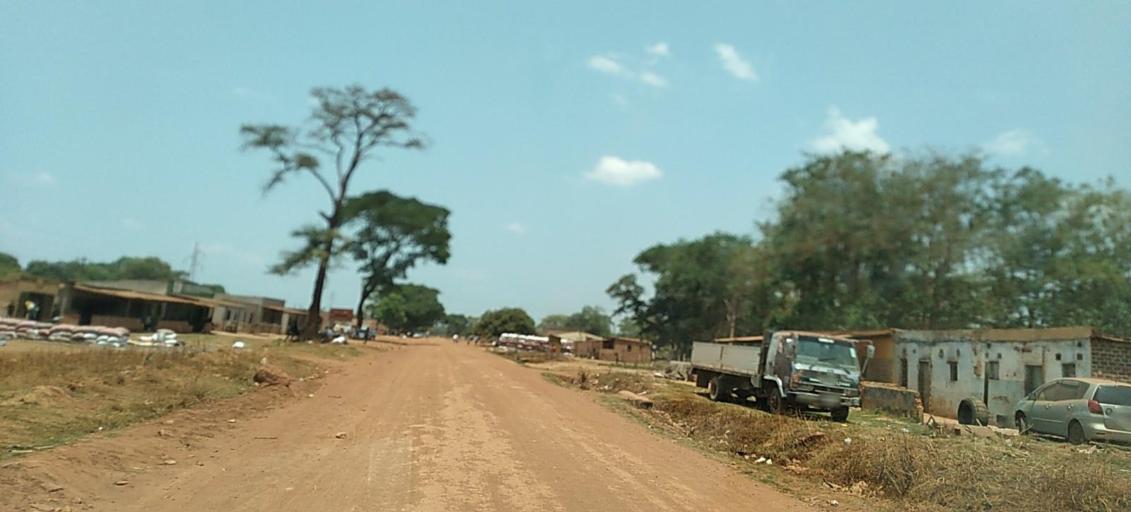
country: ZM
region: Copperbelt
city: Mpongwe
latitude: -13.5138
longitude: 28.0337
